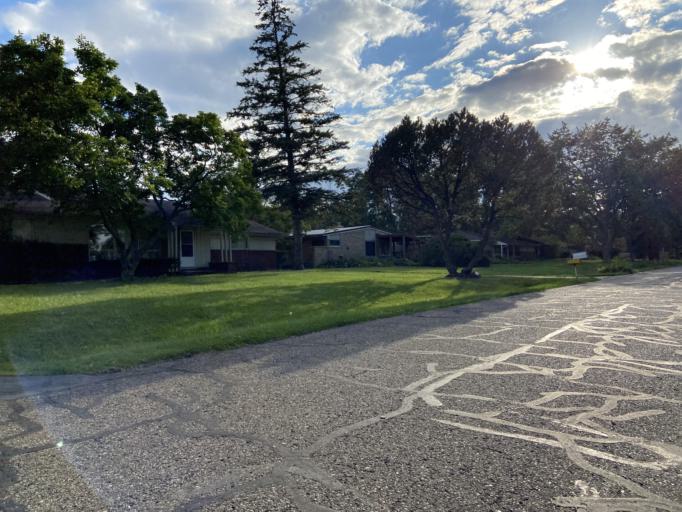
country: US
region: Michigan
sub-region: Oakland County
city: Farmington Hills
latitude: 42.5127
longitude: -83.3637
